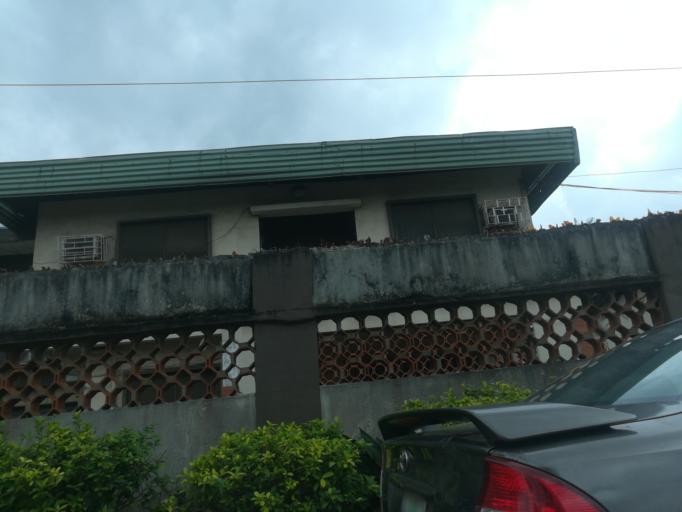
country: NG
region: Lagos
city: Somolu
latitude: 6.5548
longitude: 3.3639
